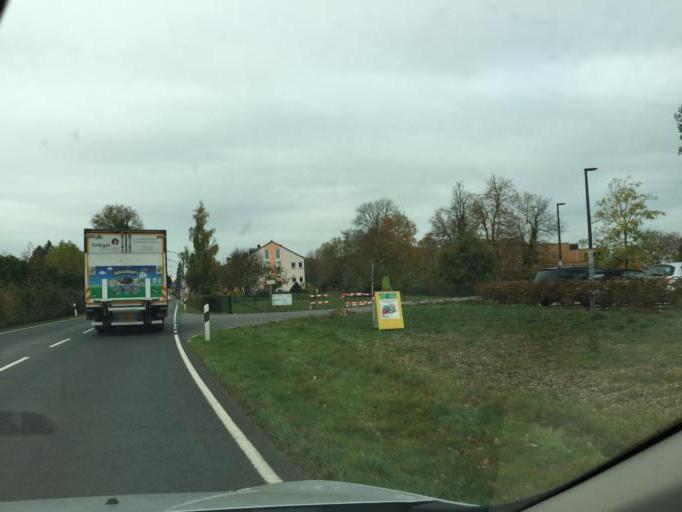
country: LU
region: Luxembourg
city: Capellen
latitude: 49.6481
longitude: 5.9878
